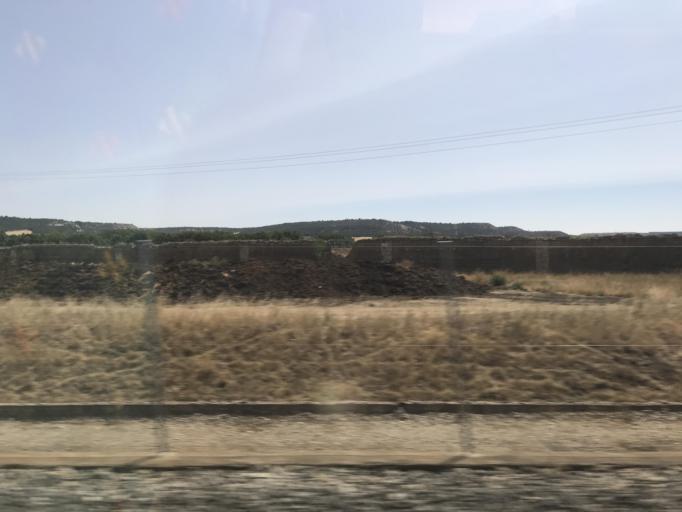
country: ES
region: Castille and Leon
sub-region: Provincia de Palencia
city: Venta de Banos
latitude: 41.9052
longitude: -4.5108
